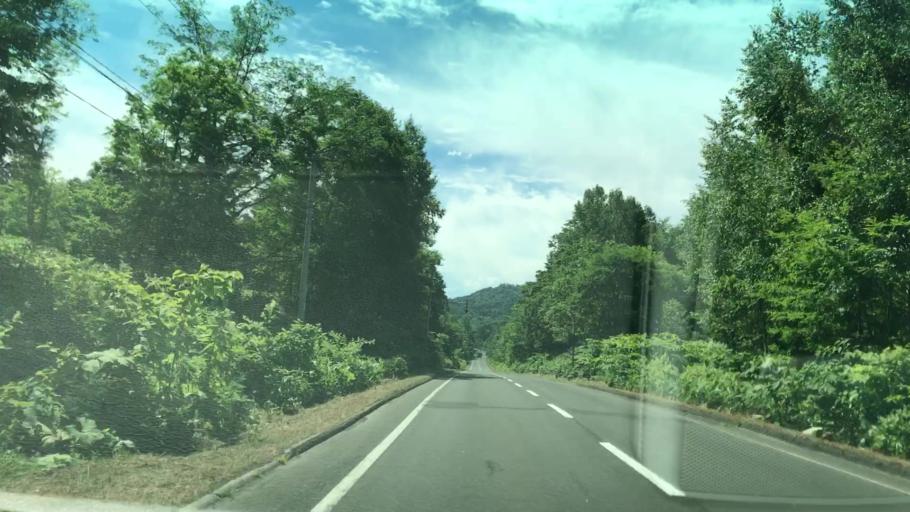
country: JP
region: Hokkaido
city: Shimo-furano
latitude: 42.9662
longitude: 142.4275
